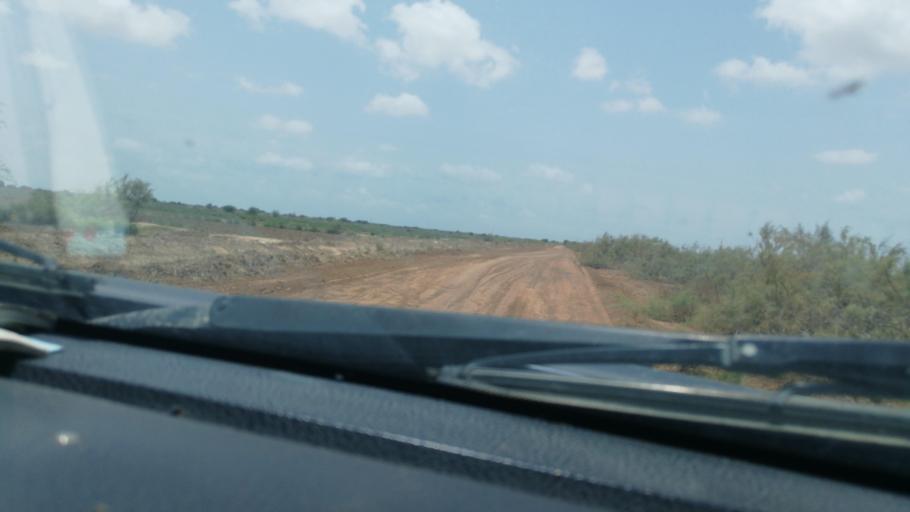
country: SN
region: Saint-Louis
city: Saint-Louis
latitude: 16.2841
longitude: -16.1941
